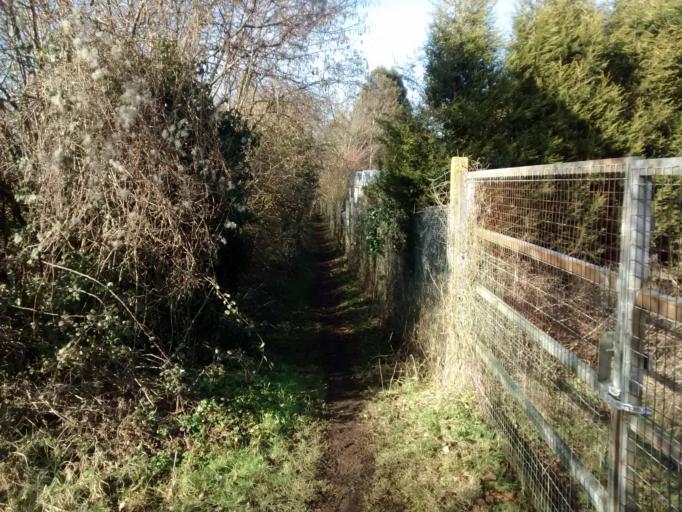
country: GB
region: England
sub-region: South Gloucestershire
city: Almondsbury
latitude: 51.5417
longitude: -2.5891
